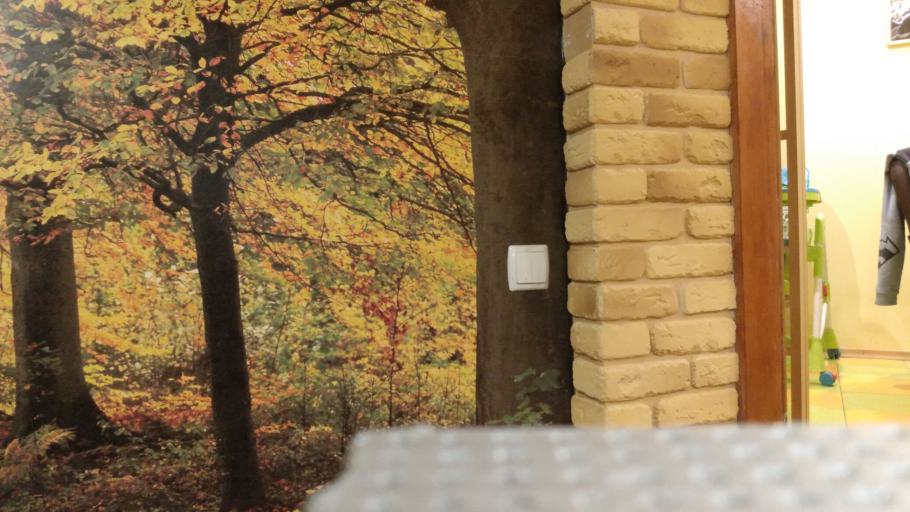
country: RU
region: Vologda
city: Babayevo
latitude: 59.3736
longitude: 35.9926
